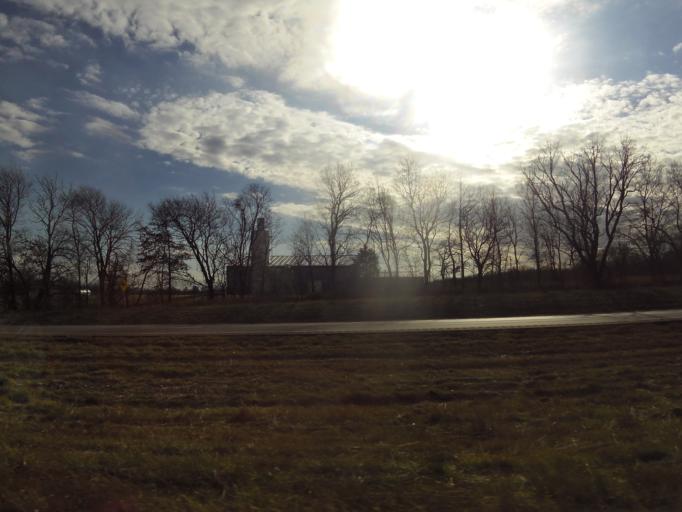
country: US
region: Missouri
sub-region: Marion County
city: Hannibal
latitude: 39.7440
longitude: -91.4374
